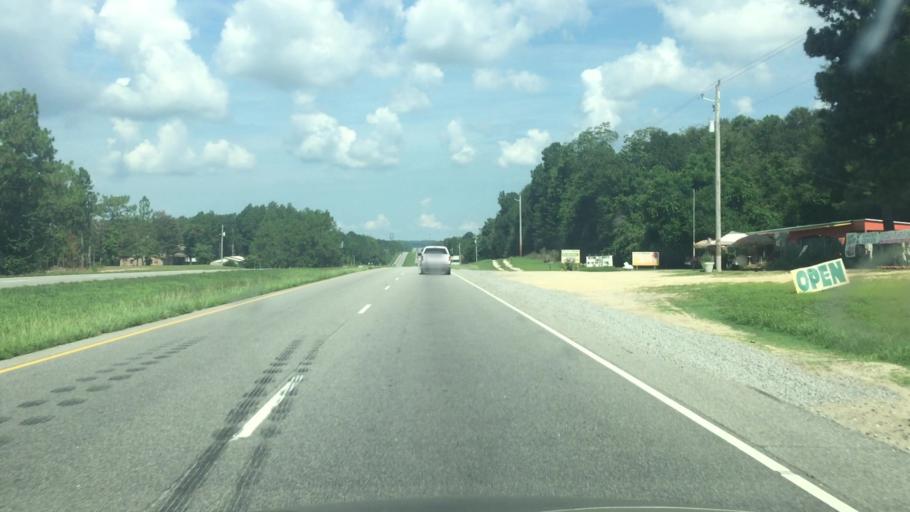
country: US
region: North Carolina
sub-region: Scotland County
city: Laurel Hill
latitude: 34.8417
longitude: -79.6045
